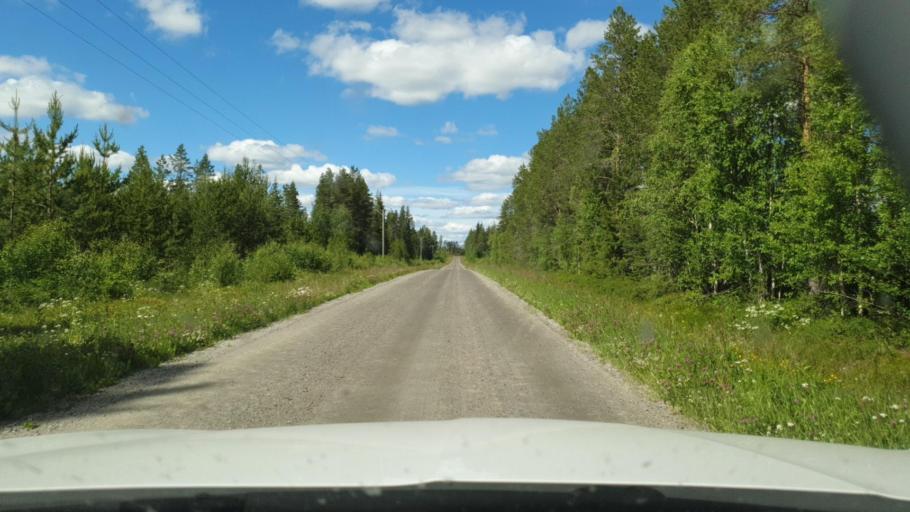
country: SE
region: Vaesterbotten
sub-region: Skelleftea Kommun
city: Backa
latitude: 65.1747
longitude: 21.0944
